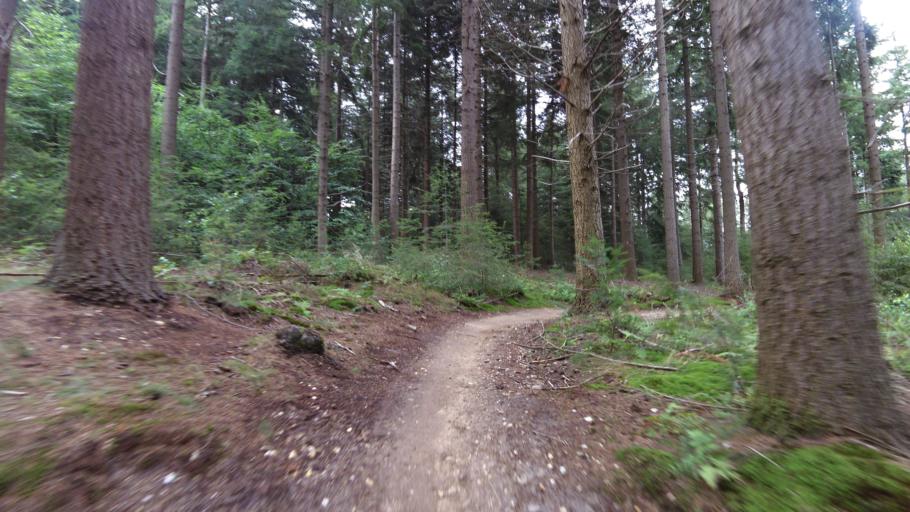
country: NL
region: Utrecht
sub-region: Gemeente Utrechtse Heuvelrug
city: Amerongen
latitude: 52.0008
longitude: 5.4854
